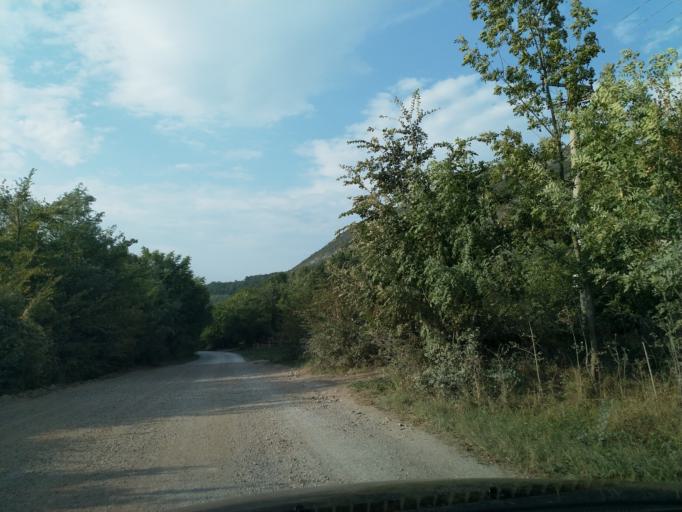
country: RS
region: Central Serbia
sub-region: Pomoravski Okrug
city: Paracin
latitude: 43.8359
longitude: 21.5404
